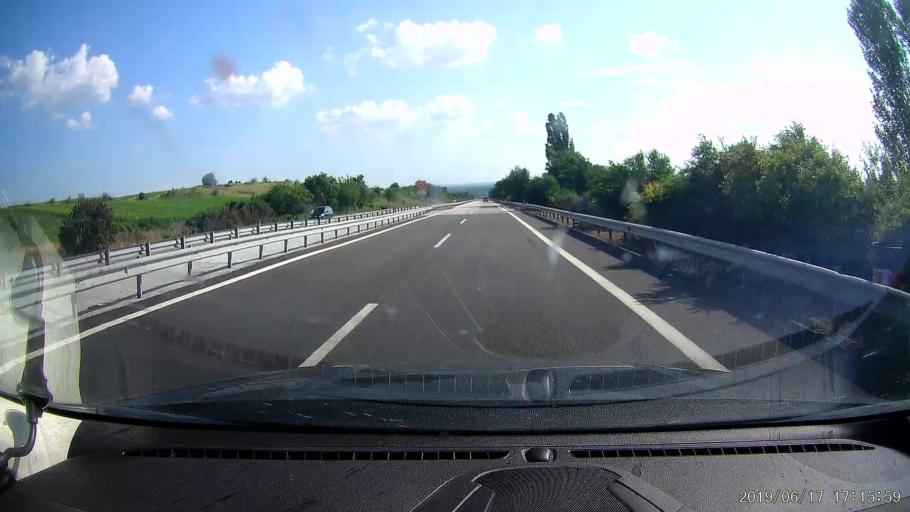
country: GR
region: East Macedonia and Thrace
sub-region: Nomos Evrou
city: Kastanies
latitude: 41.6980
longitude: 26.4866
